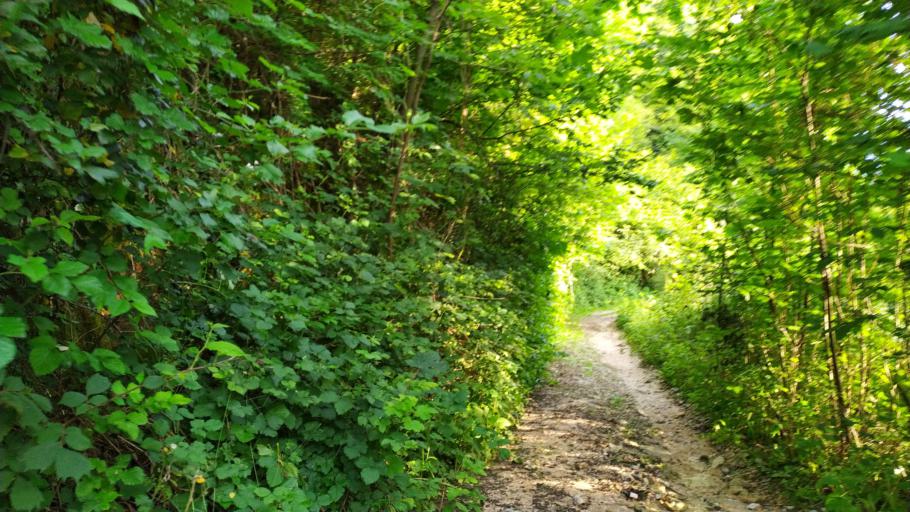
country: IT
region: Veneto
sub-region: Provincia di Vicenza
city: San Quirico
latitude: 45.6858
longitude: 11.2781
